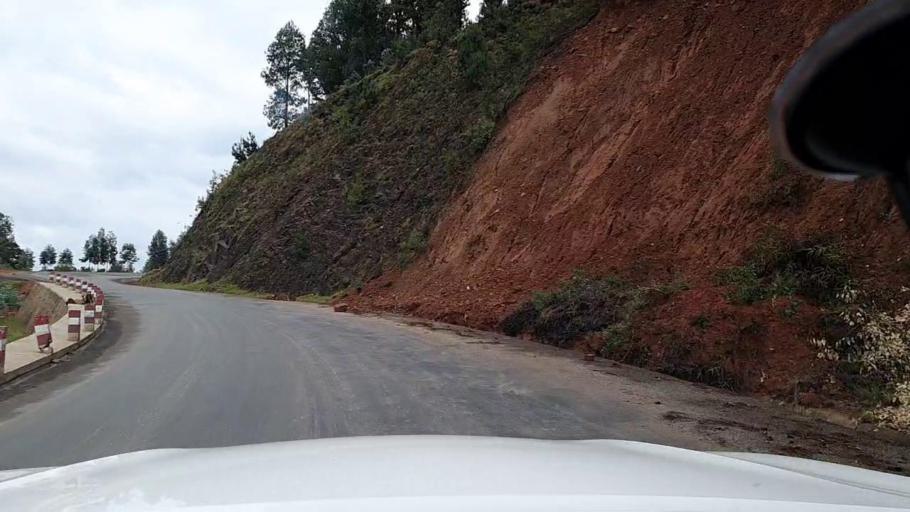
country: RW
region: Southern Province
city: Gitarama
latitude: -2.0646
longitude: 29.5604
